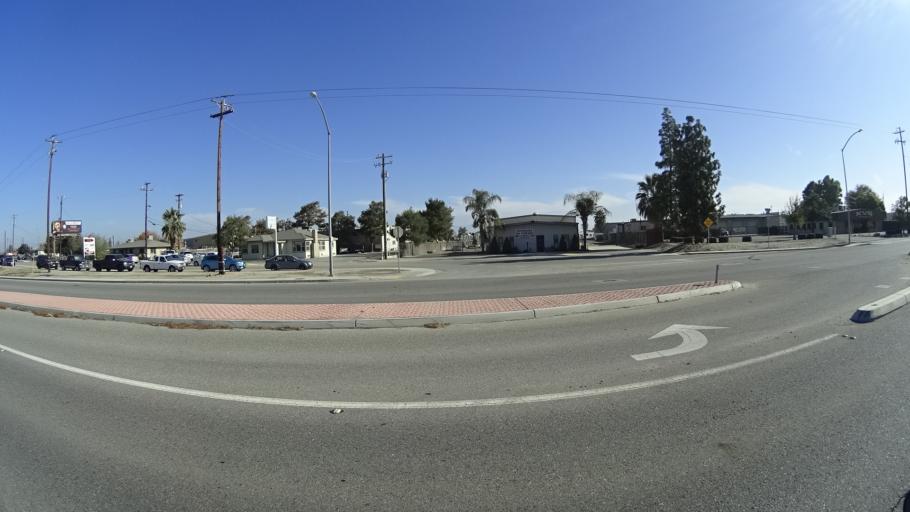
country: US
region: California
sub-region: Kern County
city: Rosedale
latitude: 35.3951
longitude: -119.1459
